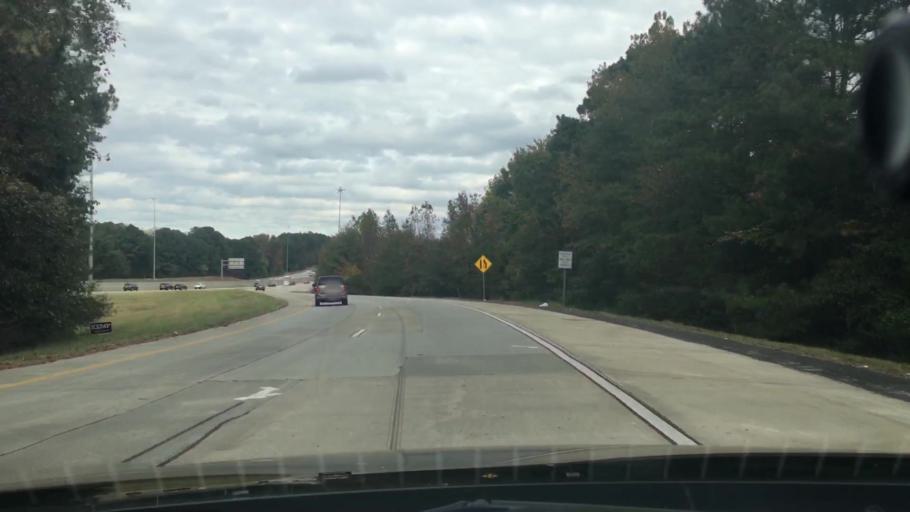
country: US
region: Georgia
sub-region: Fulton County
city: Palmetto
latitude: 33.4427
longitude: -84.6926
